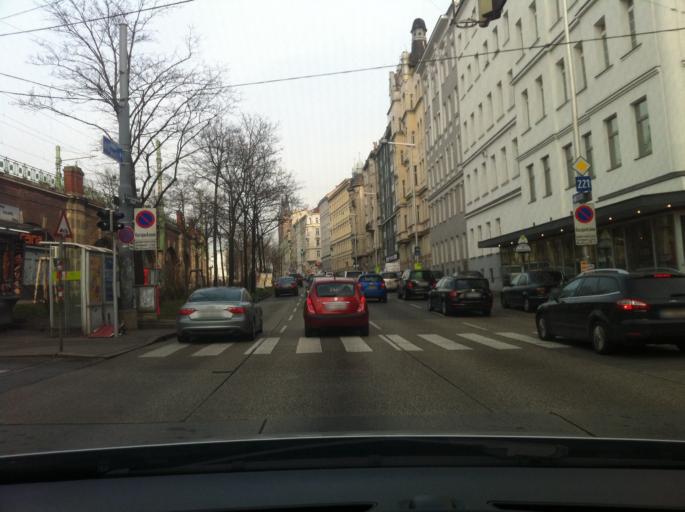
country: AT
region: Vienna
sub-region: Wien Stadt
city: Vienna
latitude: 48.2084
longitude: 16.3388
